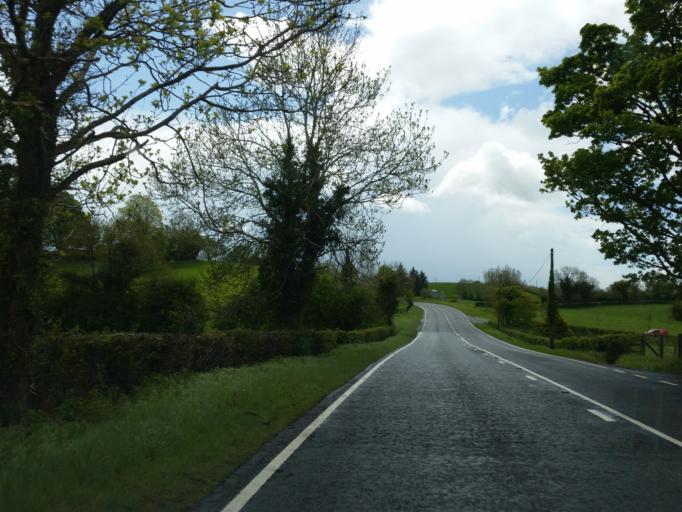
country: GB
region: Northern Ireland
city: Lisnaskea
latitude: 54.2782
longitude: -7.4669
